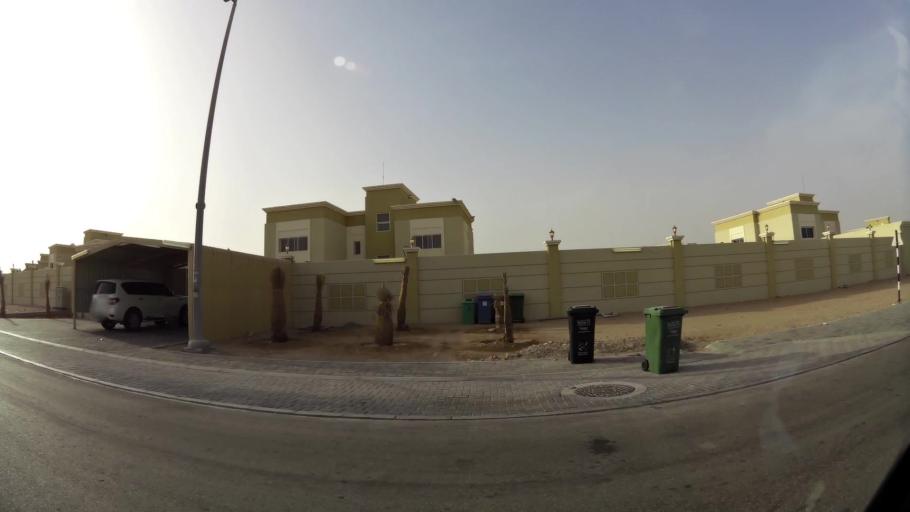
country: AE
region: Abu Dhabi
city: Al Ain
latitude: 24.1161
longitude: 55.7068
